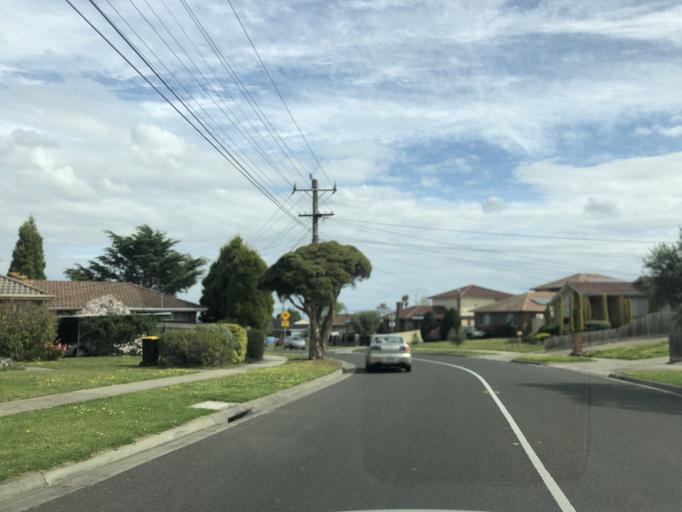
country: AU
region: Victoria
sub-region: Greater Dandenong
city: Noble Park North
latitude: -37.9541
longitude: 145.1992
